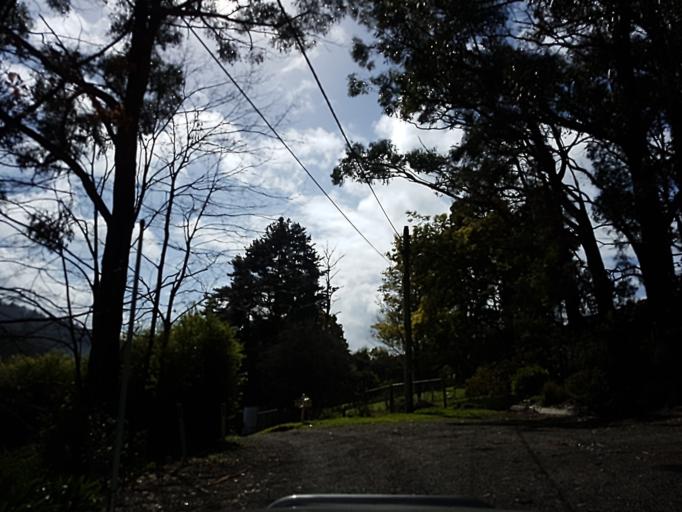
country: AU
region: Victoria
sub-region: Yarra Ranges
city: Monbulk
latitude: -37.8886
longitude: 145.3970
